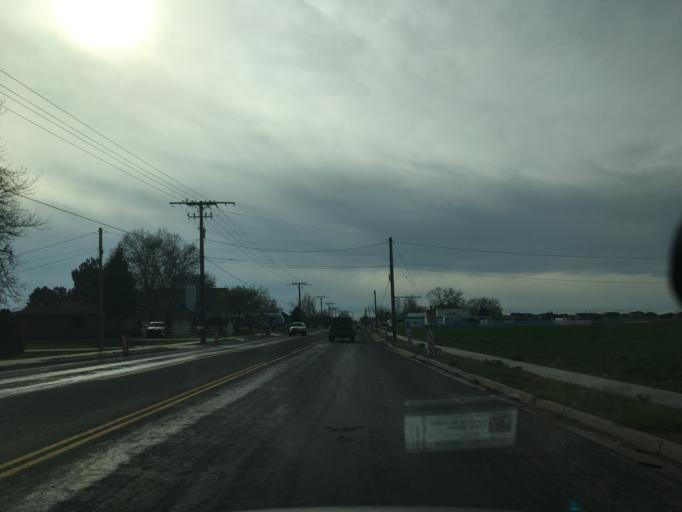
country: US
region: Utah
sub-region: Davis County
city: Layton
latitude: 41.0602
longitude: -111.9884
